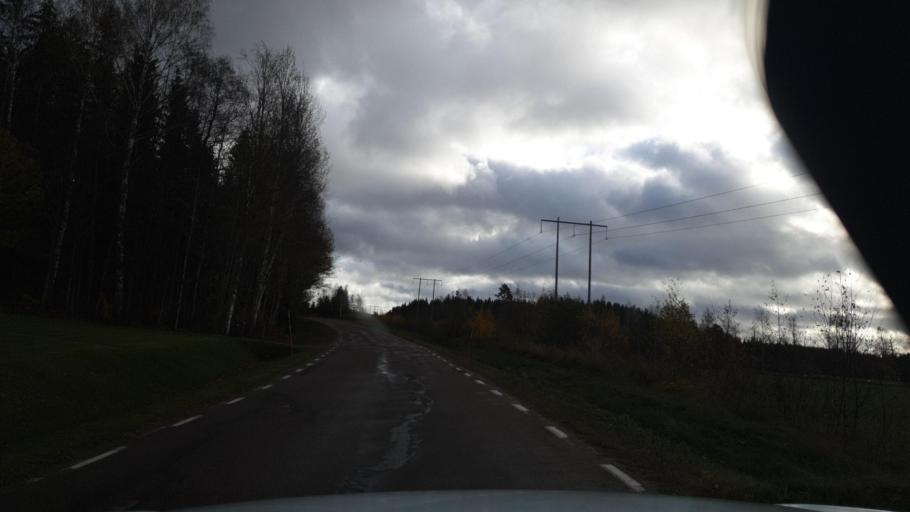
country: SE
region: Vaermland
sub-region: Arvika Kommun
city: Arvika
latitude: 59.4875
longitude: 12.7482
